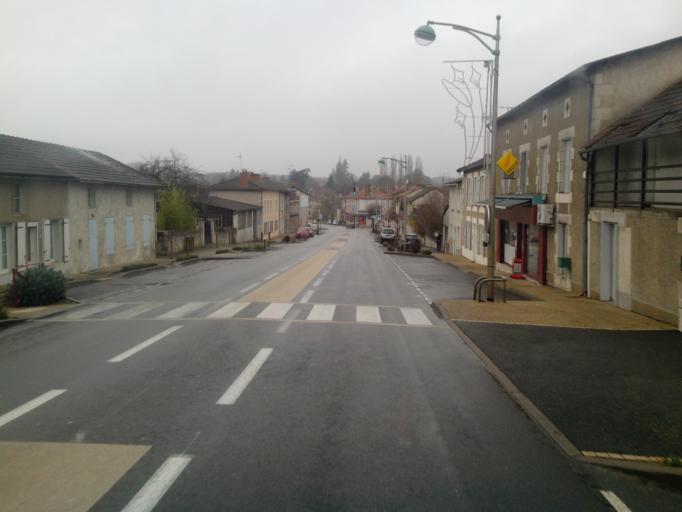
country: FR
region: Poitou-Charentes
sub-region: Departement de la Vienne
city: Terce
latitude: 46.4350
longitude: 0.5995
